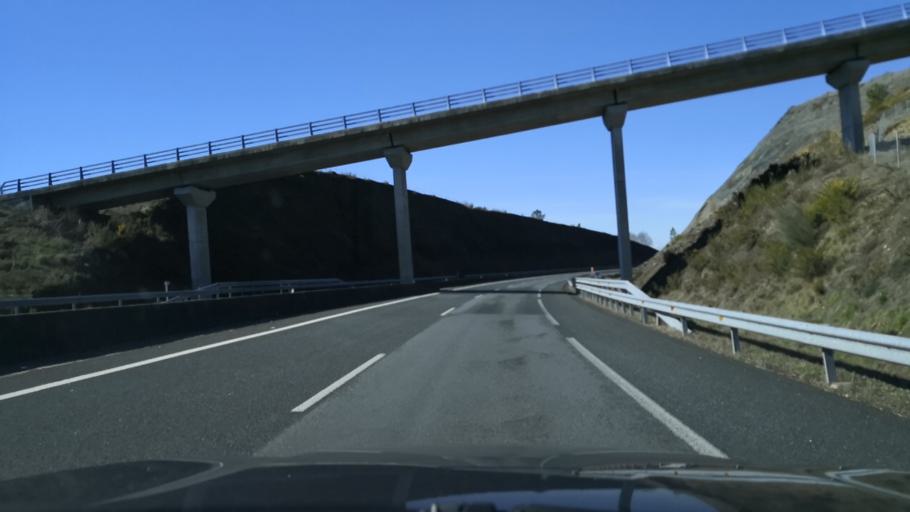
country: ES
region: Galicia
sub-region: Provincia de Pontevedra
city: Dozon
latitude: 42.5885
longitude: -8.0801
